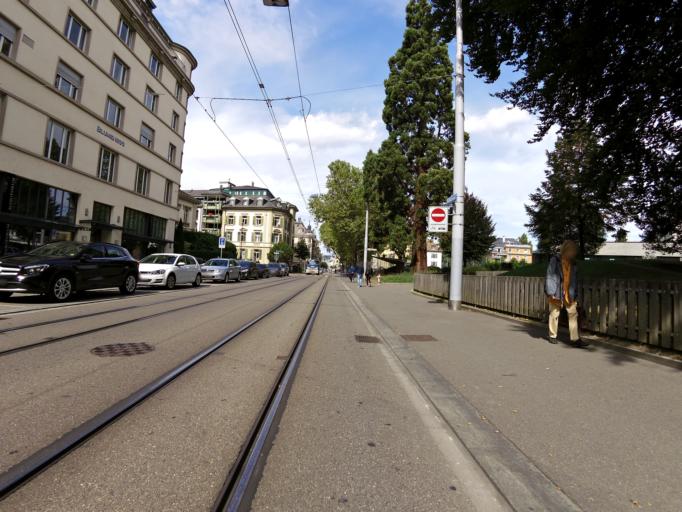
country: CH
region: Zurich
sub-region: Bezirk Zuerich
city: Zuerich (Kreis 8) / Muehlebach
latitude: 47.3591
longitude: 8.5534
